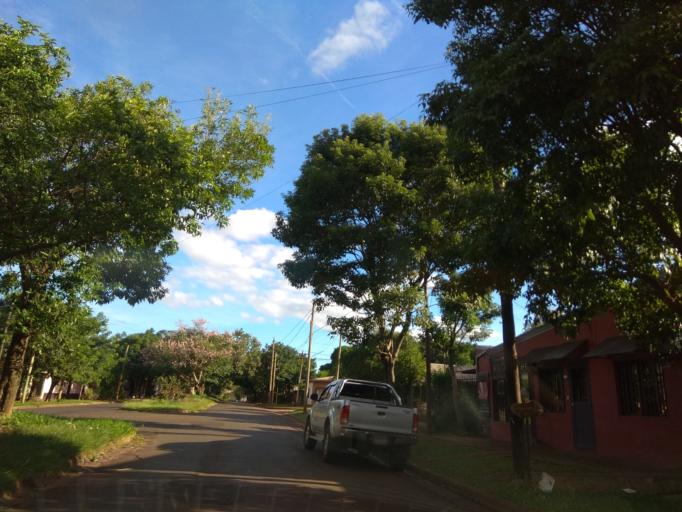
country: AR
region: Misiones
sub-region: Departamento de Capital
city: Posadas
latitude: -27.3729
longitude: -55.9250
